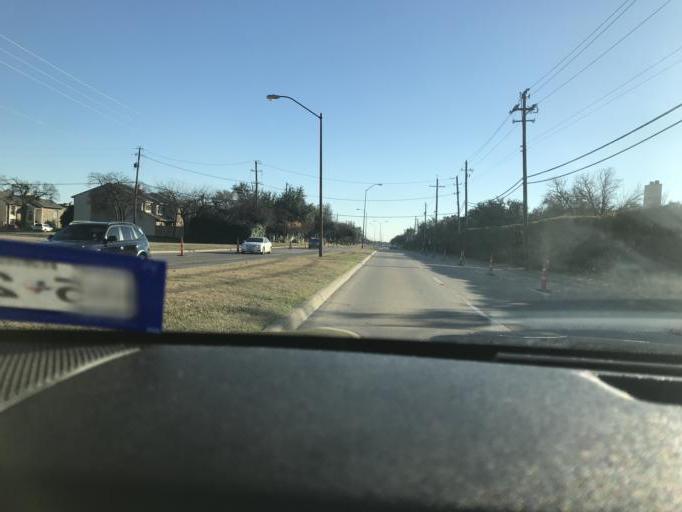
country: US
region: Texas
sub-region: Dallas County
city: Richardson
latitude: 32.9199
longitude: -96.7355
